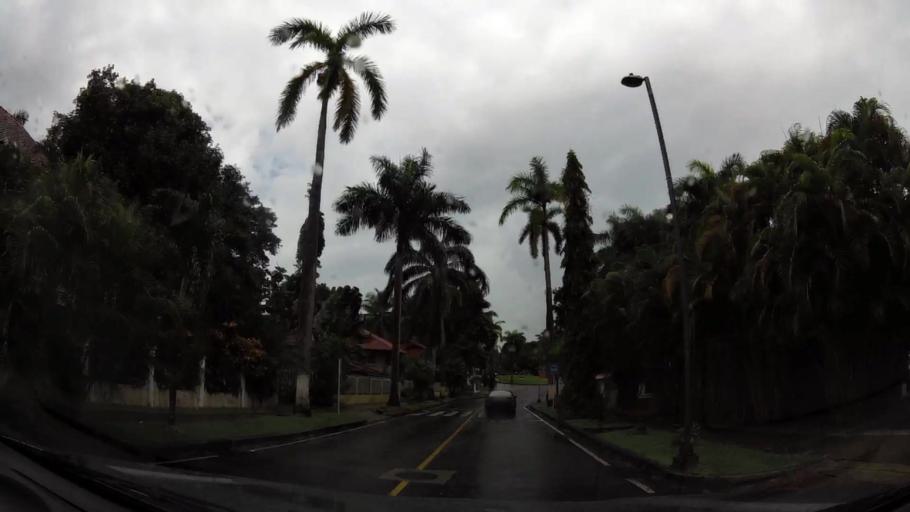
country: PA
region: Panama
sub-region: Distrito de Panama
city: Ancon
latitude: 8.9788
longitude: -79.5590
